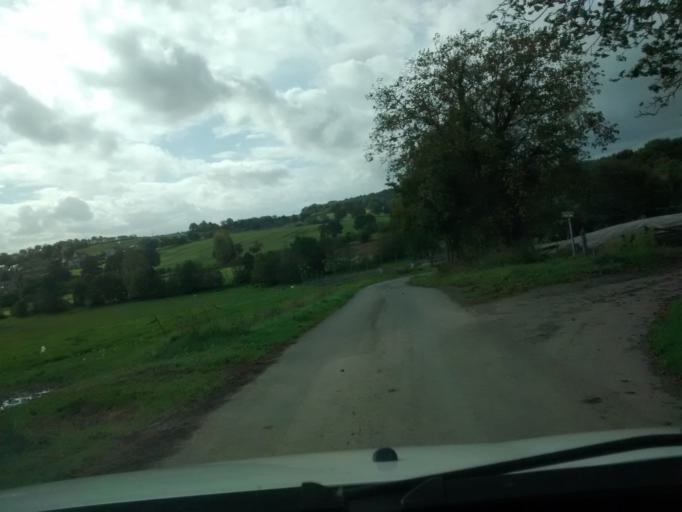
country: FR
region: Brittany
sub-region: Departement d'Ille-et-Vilaine
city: Poce-les-Bois
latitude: 48.1527
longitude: -1.3050
